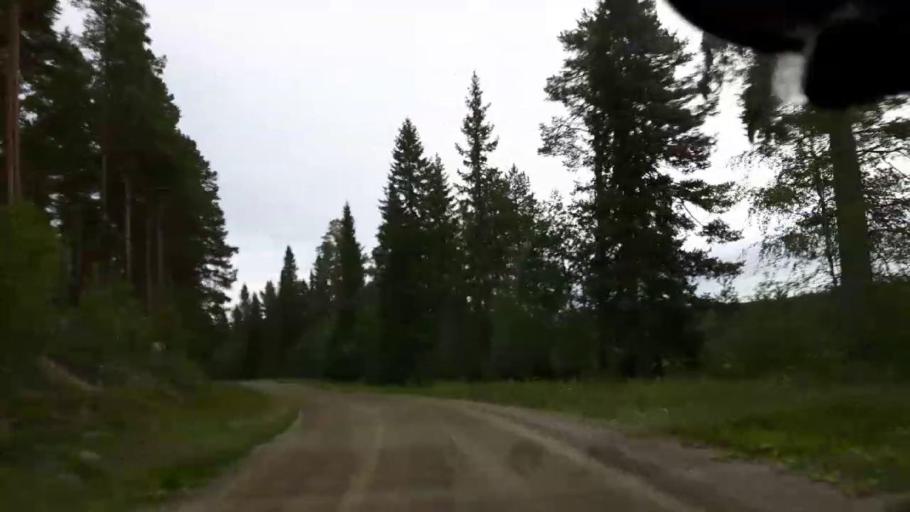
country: SE
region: Jaemtland
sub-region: Braecke Kommun
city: Braecke
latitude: 62.9316
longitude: 15.4823
